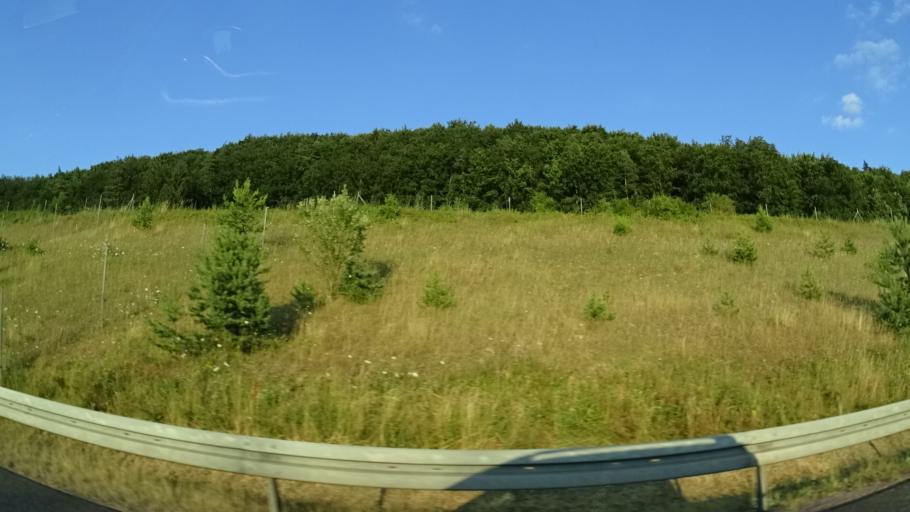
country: DE
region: Thuringia
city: Ellingshausen
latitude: 50.5430
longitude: 10.4789
